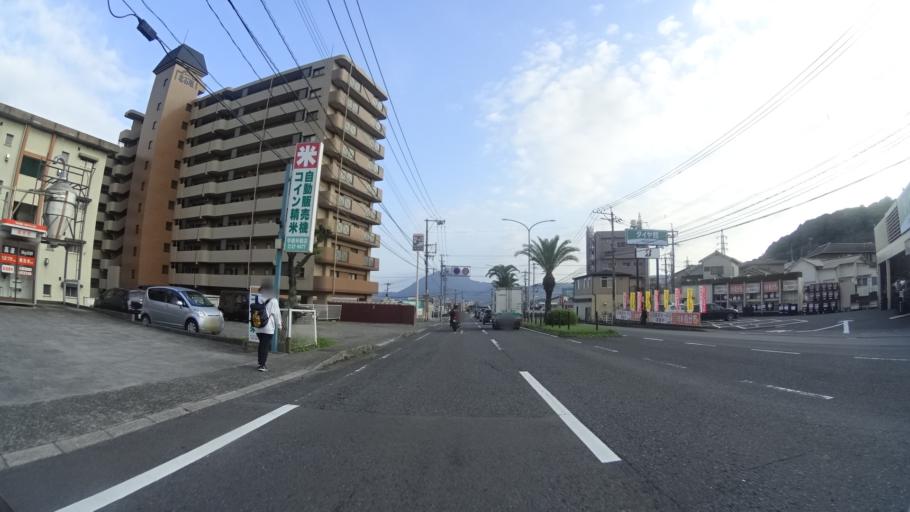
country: JP
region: Oita
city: Beppu
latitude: 33.3076
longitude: 131.4882
